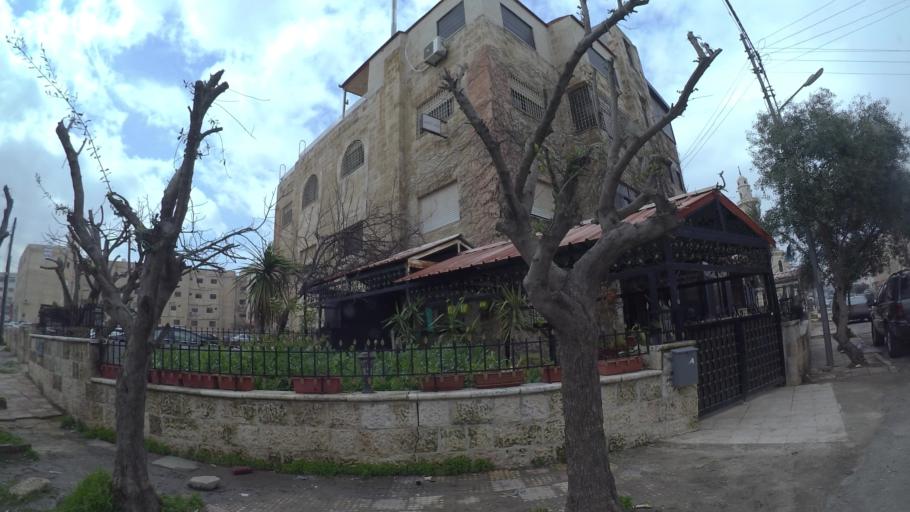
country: JO
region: Amman
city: Umm as Summaq
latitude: 31.8935
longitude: 35.8440
